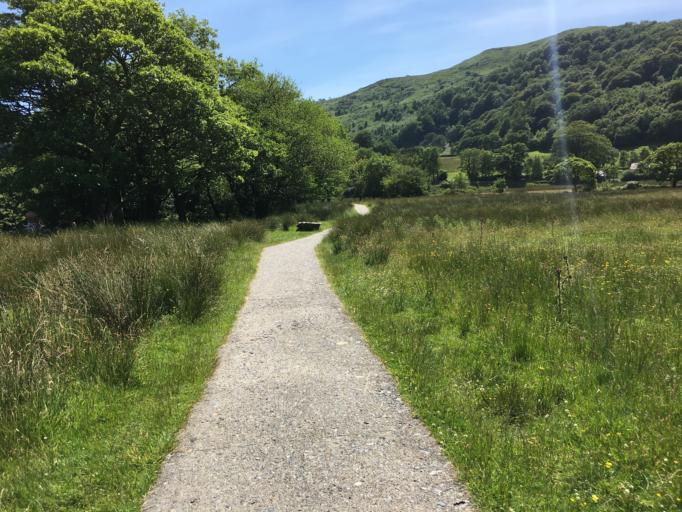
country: GB
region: Wales
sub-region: Gwynedd
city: Penrhyndeudraeth
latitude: 53.0074
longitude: -4.1003
